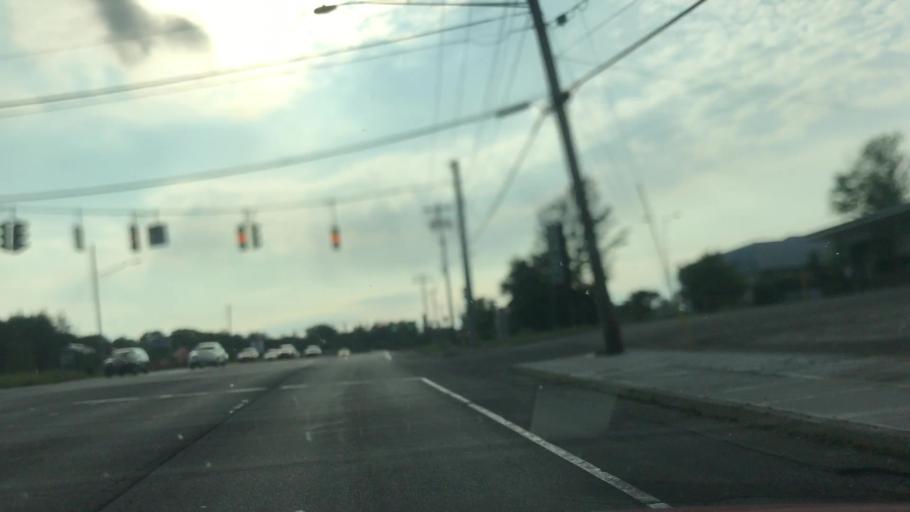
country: US
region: New York
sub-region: Albany County
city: Watervliet
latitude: 42.7382
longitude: -73.7306
